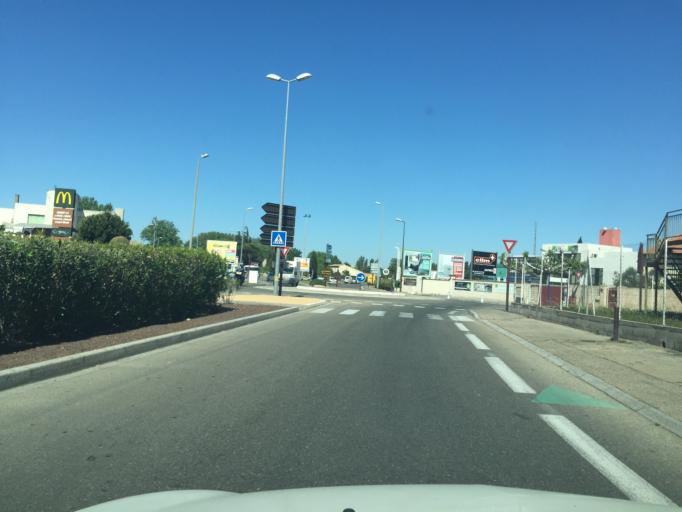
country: FR
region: Provence-Alpes-Cote d'Azur
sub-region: Departement du Vaucluse
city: Avignon
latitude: 43.9399
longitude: 4.8374
